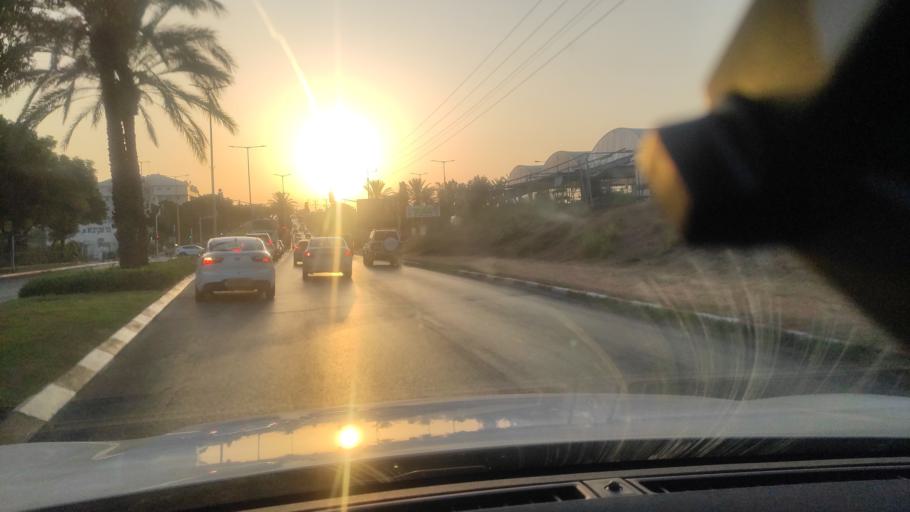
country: IL
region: Central District
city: Kfar Saba
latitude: 32.1840
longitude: 34.9181
